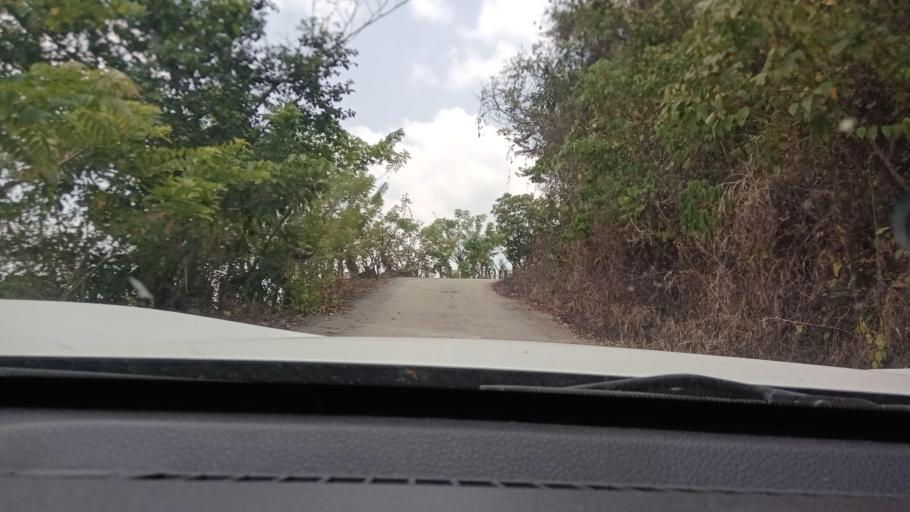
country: MX
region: Tabasco
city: Chontalpa
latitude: 17.5505
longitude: -93.7386
